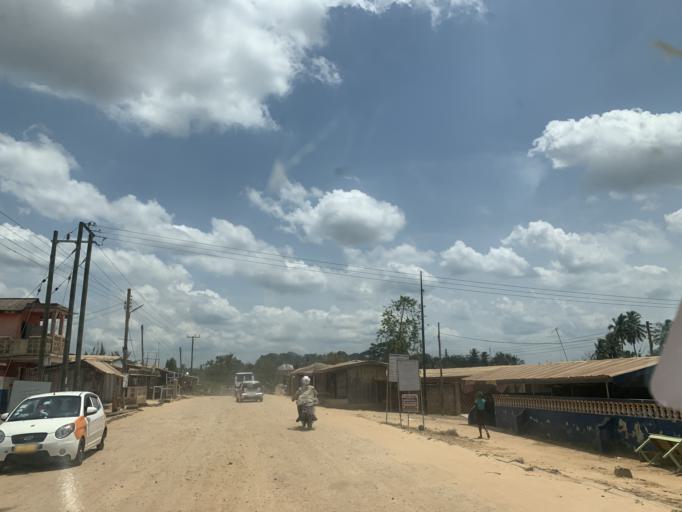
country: GH
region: Central
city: Swedru
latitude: 5.5110
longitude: -0.6944
